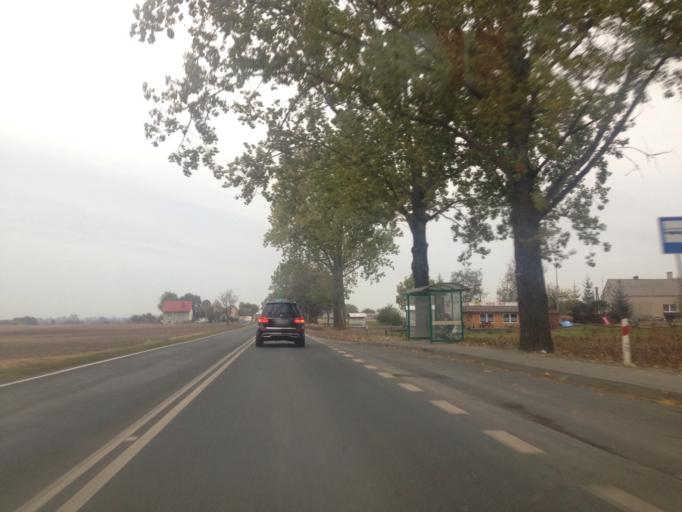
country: PL
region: Greater Poland Voivodeship
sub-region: Powiat gnieznienski
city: Niechanowo
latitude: 52.5531
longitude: 17.7133
